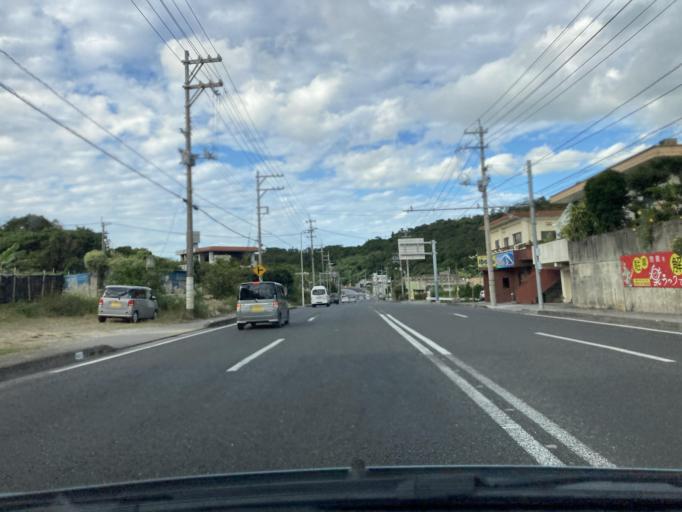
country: JP
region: Okinawa
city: Ishikawa
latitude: 26.3941
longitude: 127.8325
